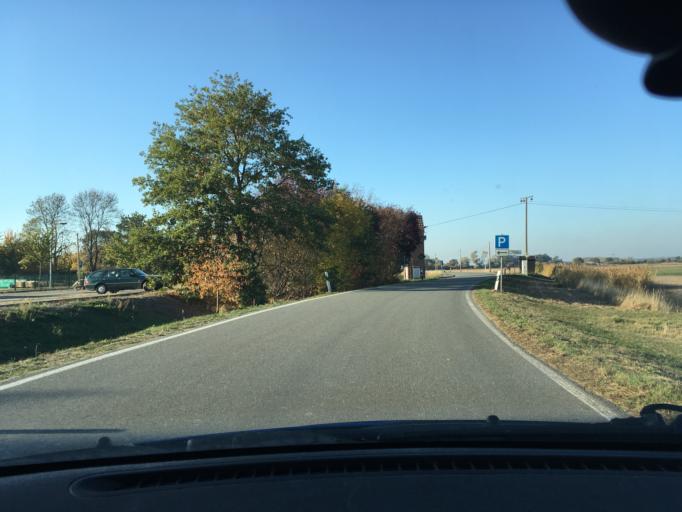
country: DE
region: Lower Saxony
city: Hitzacker
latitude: 53.1619
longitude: 11.0517
